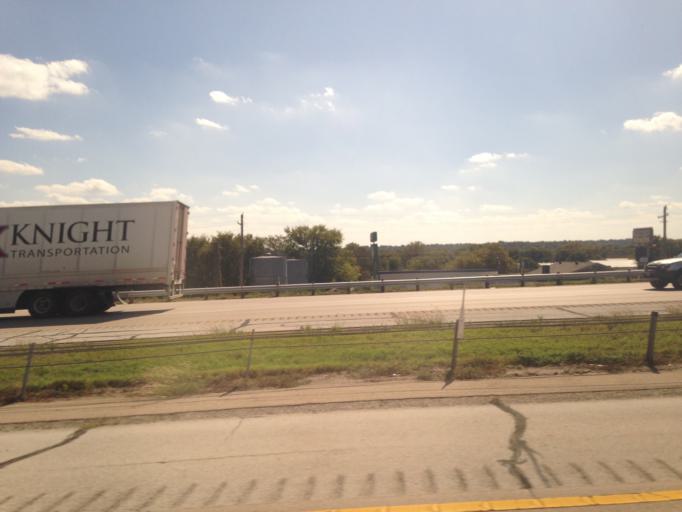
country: US
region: Texas
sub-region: Parker County
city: Aledo
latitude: 32.7210
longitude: -97.5304
